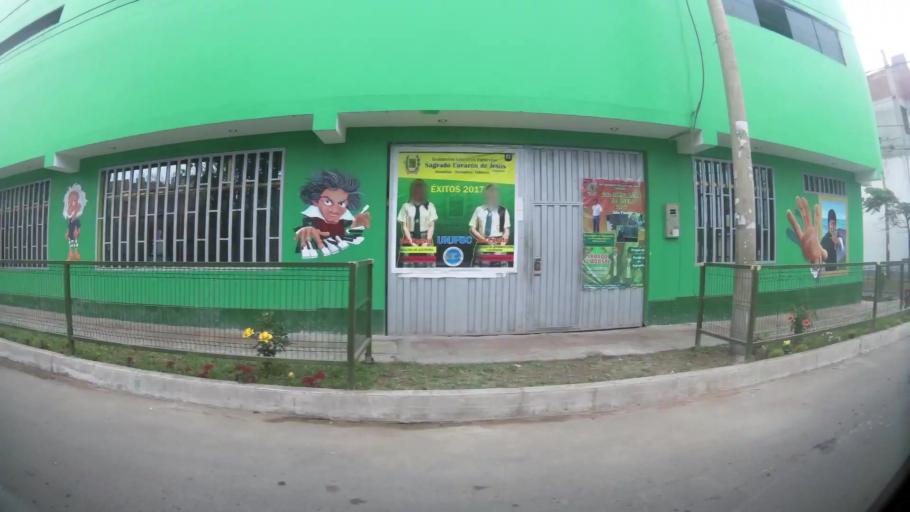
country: PE
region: Lima
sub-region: Provincia de Huaral
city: Chancay
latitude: -11.5696
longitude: -77.2697
